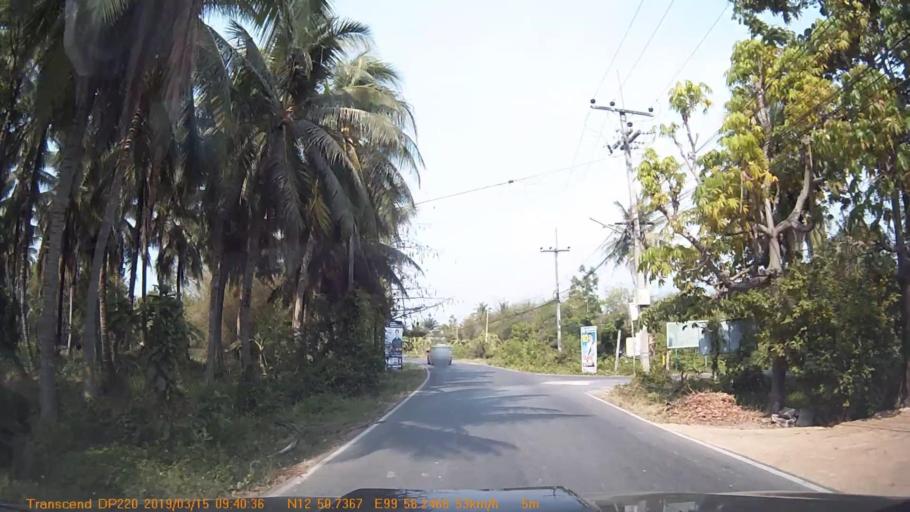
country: TH
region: Phetchaburi
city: Cha-am
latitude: 12.8456
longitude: 99.9374
